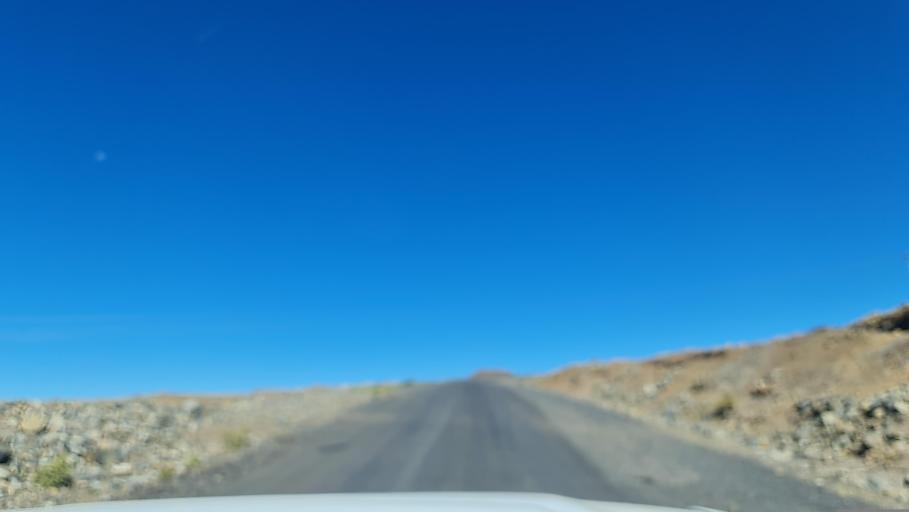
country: ET
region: Amhara
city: Debark'
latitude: 13.1538
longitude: 38.1871
